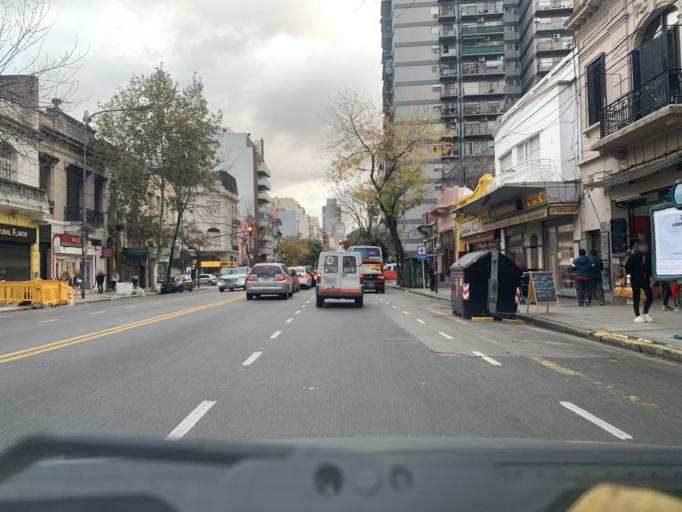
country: AR
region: Buenos Aires F.D.
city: Colegiales
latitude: -34.5774
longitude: -58.4491
